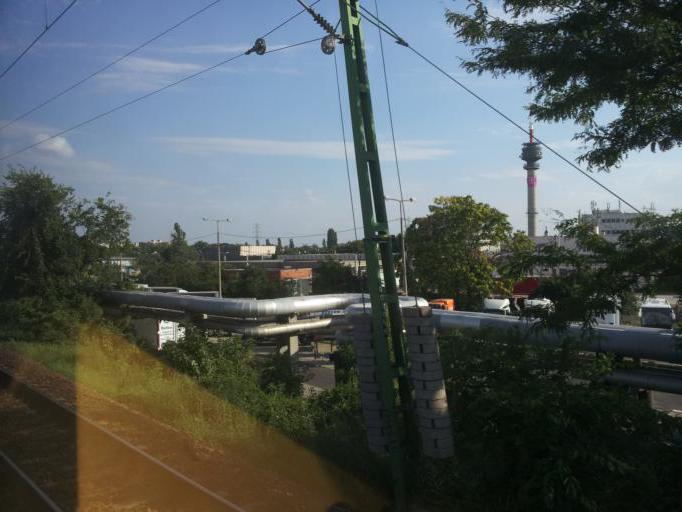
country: HU
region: Budapest
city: Budapest XIX. keruelet
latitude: 47.4735
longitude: 19.1276
